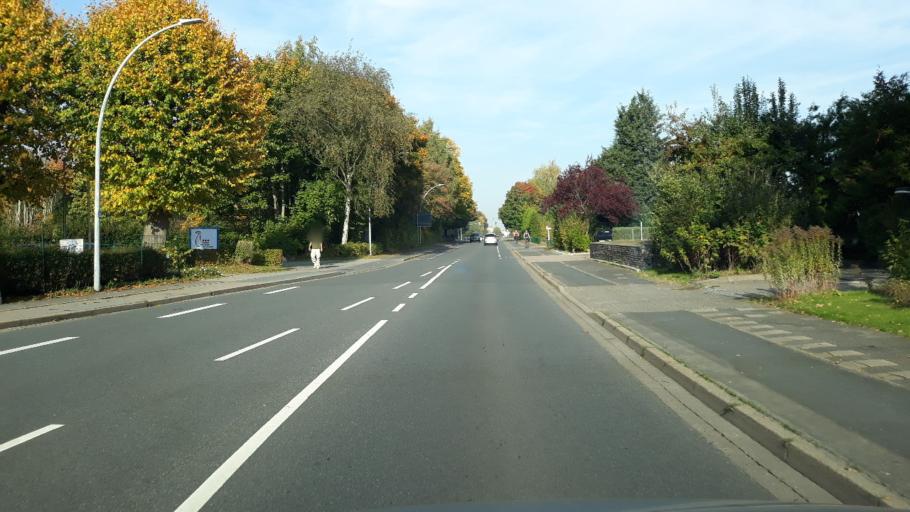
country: DE
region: Schleswig-Holstein
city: Schleswig
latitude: 54.5261
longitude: 9.5701
